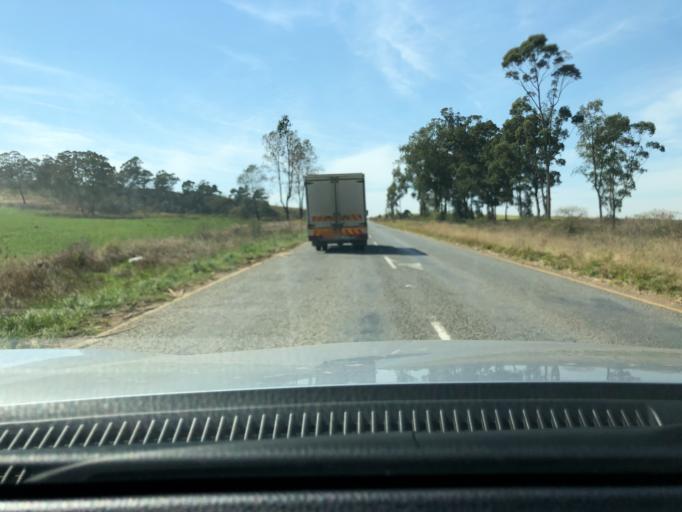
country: ZA
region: KwaZulu-Natal
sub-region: uMgungundlovu District Municipality
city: Camperdown
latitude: -29.7222
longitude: 30.4792
